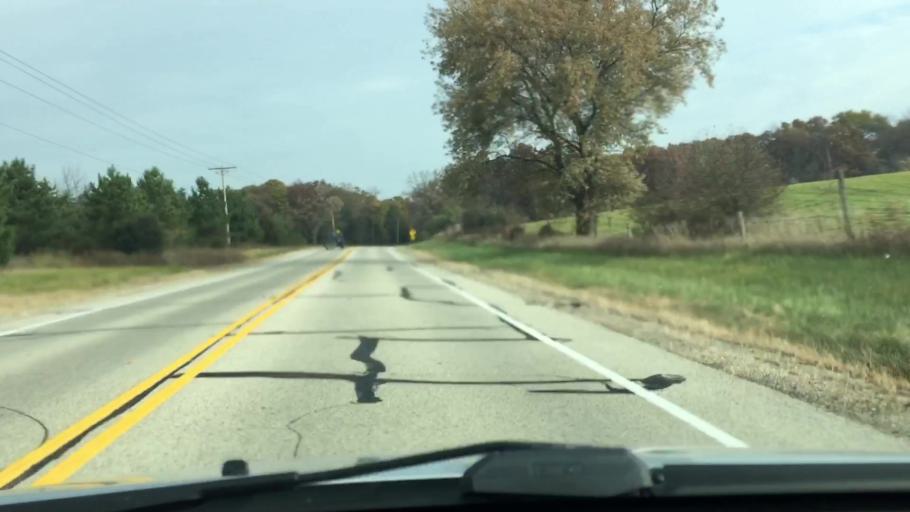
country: US
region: Wisconsin
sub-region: Waukesha County
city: Dousman
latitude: 42.9797
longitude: -88.4662
